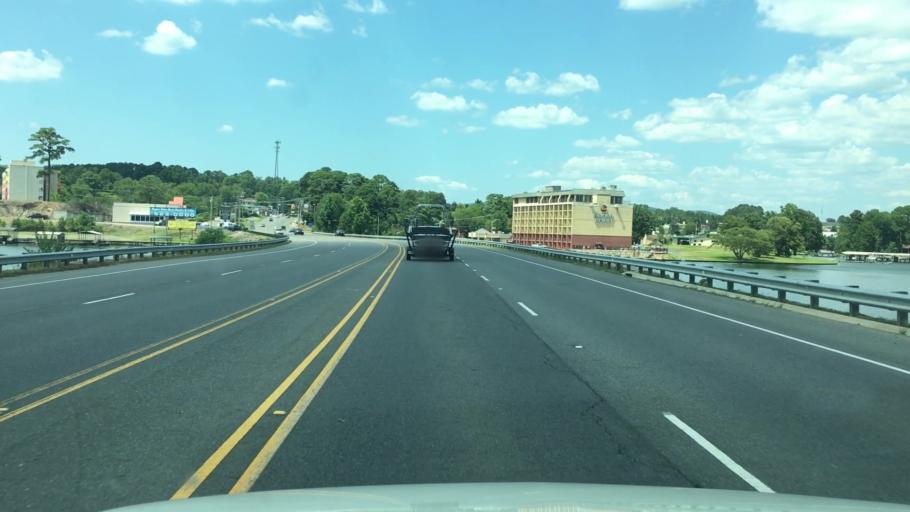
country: US
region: Arkansas
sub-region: Garland County
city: Lake Hamilton
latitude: 34.4403
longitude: -93.0885
